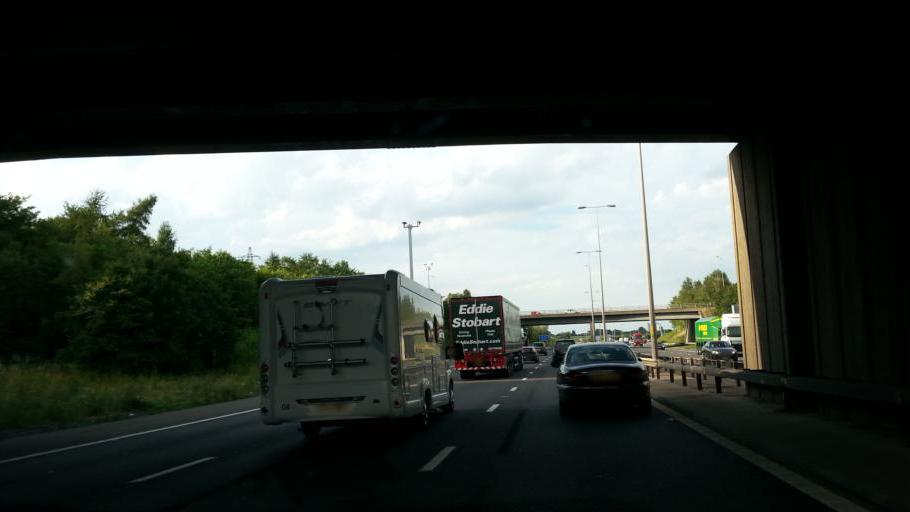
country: GB
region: England
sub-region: Worcestershire
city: Fernhill Heath
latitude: 52.2120
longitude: -2.1584
